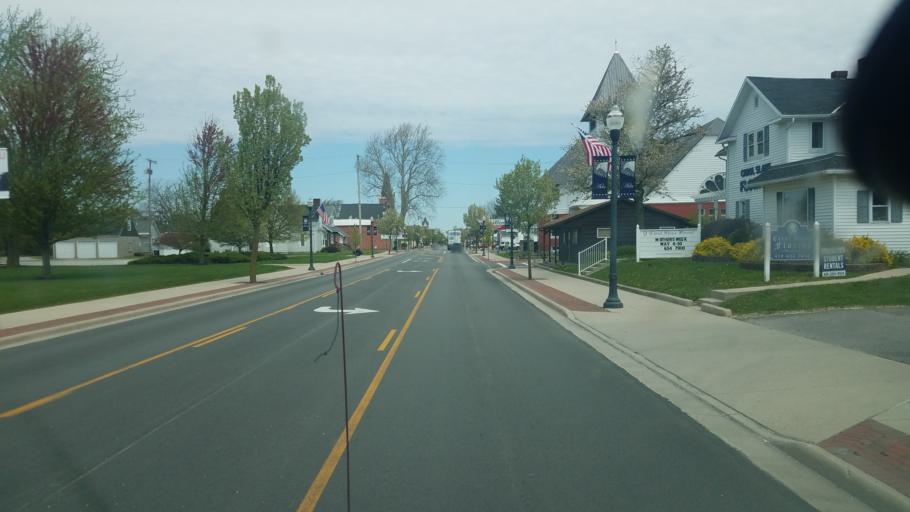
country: US
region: Ohio
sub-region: Hardin County
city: Ada
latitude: 40.7672
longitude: -83.8232
